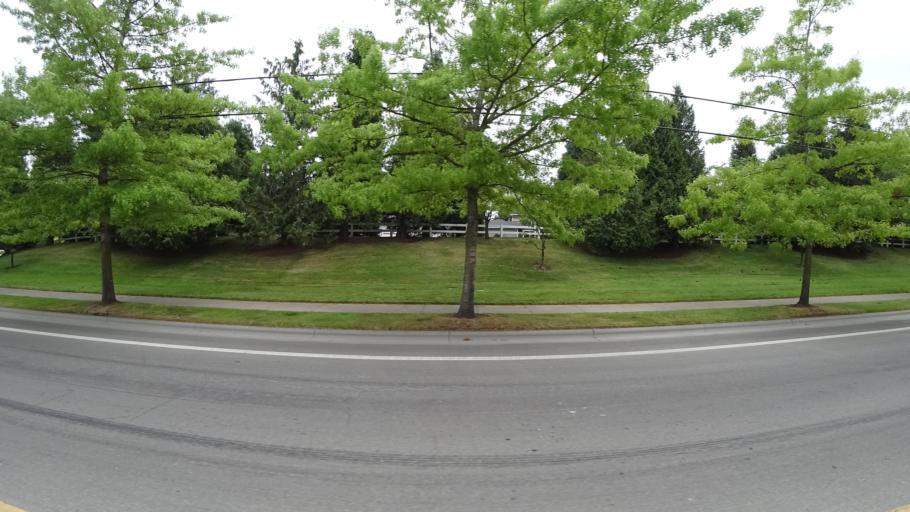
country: US
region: Oregon
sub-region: Washington County
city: Hillsboro
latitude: 45.4949
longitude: -122.9692
